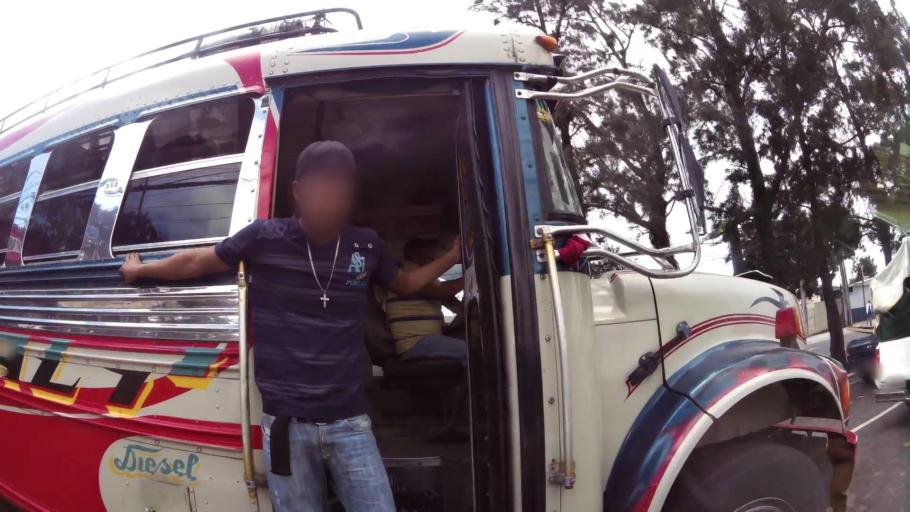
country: GT
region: Guatemala
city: Mixco
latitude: 14.6366
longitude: -90.5623
